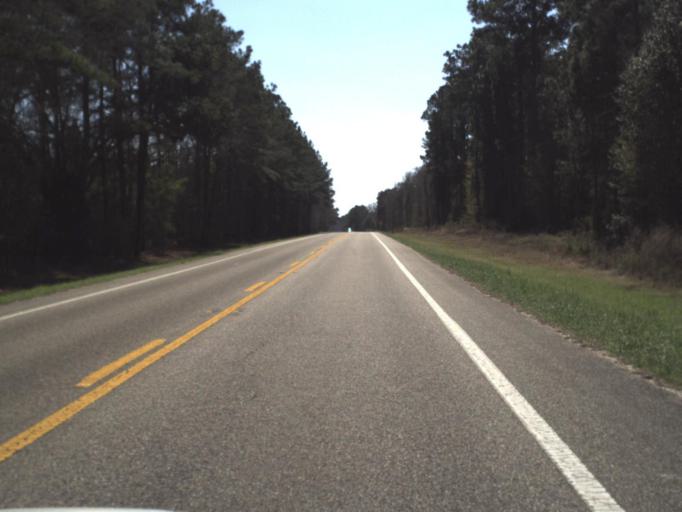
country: US
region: Florida
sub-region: Calhoun County
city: Blountstown
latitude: 30.5420
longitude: -85.0271
